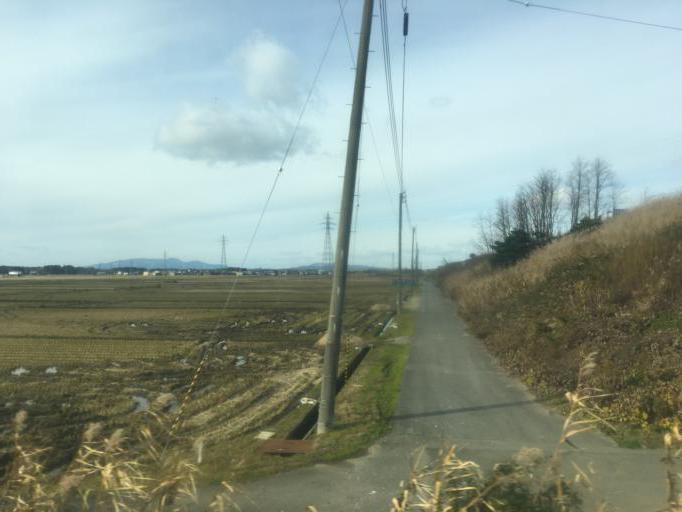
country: JP
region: Akita
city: Tenno
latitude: 39.8608
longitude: 140.0584
